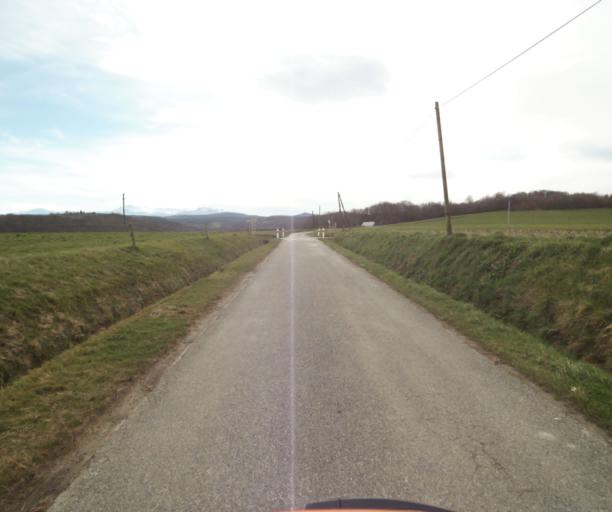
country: FR
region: Midi-Pyrenees
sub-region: Departement de l'Ariege
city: Verniolle
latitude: 43.0813
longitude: 1.7104
